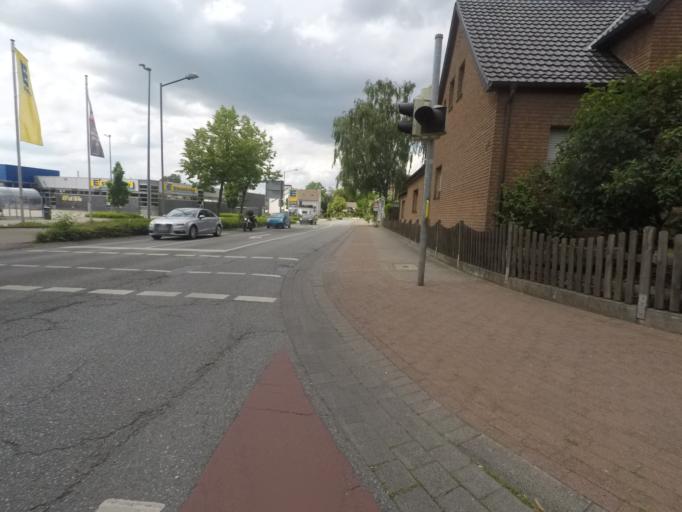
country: DE
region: North Rhine-Westphalia
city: Buende
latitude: 52.1880
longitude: 8.6004
